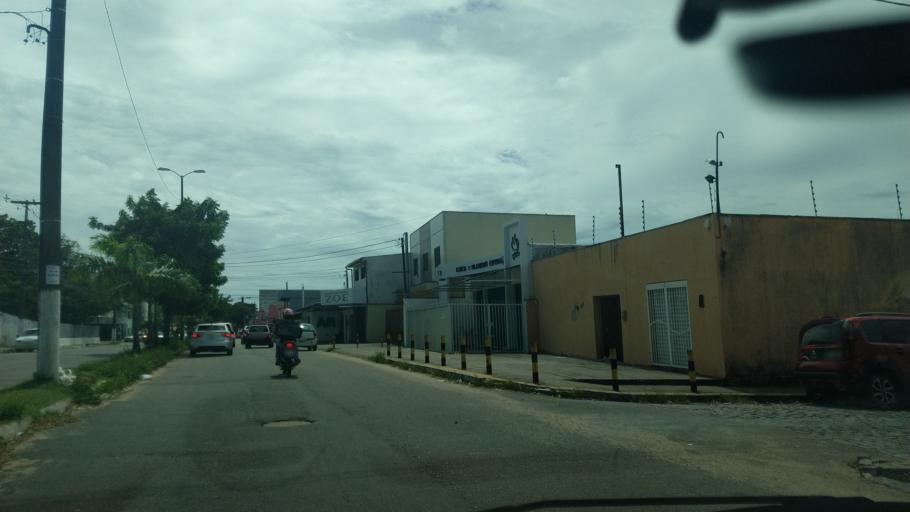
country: BR
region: Rio Grande do Norte
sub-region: Natal
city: Natal
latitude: -5.8256
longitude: -35.2344
